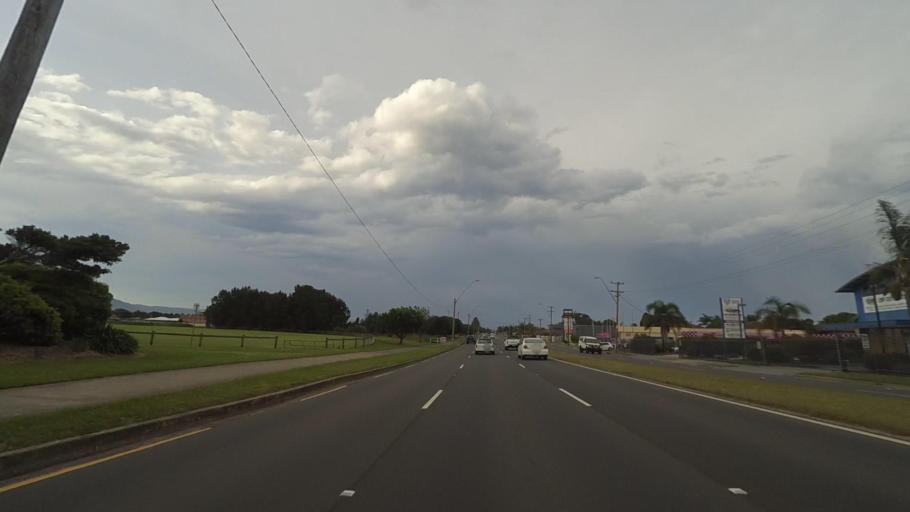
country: AU
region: New South Wales
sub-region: Shellharbour
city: Lake Illawarra
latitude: -34.5455
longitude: 150.8622
